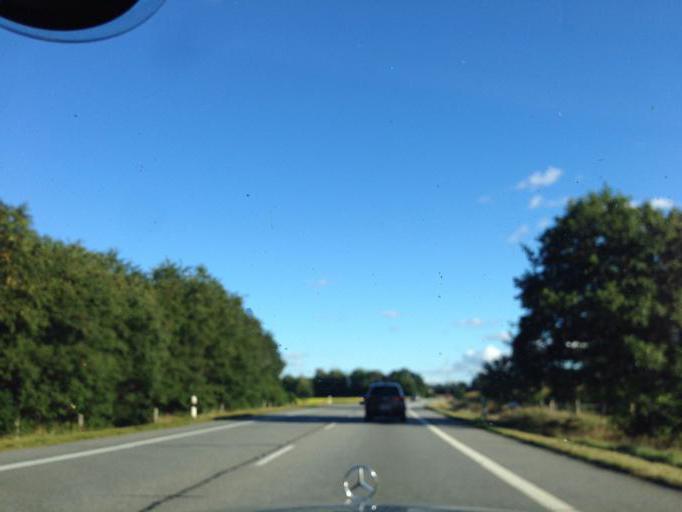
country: DE
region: Schleswig-Holstein
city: Rickling
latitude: 54.0130
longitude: 10.1709
